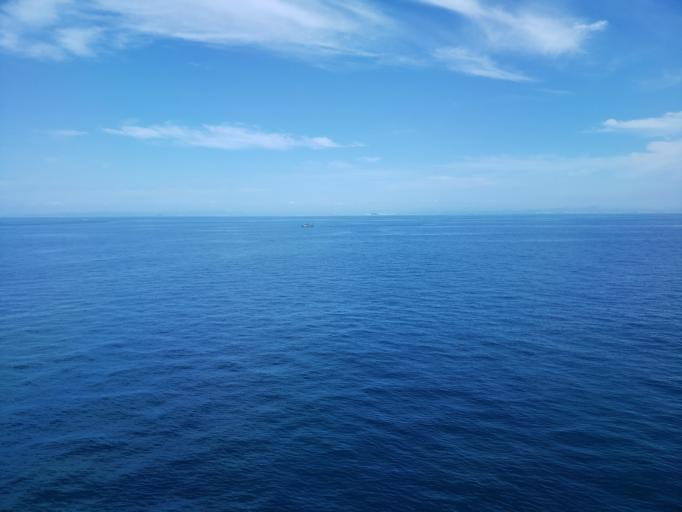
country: JP
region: Hyogo
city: Kakogawacho-honmachi
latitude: 34.5566
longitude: 134.7560
